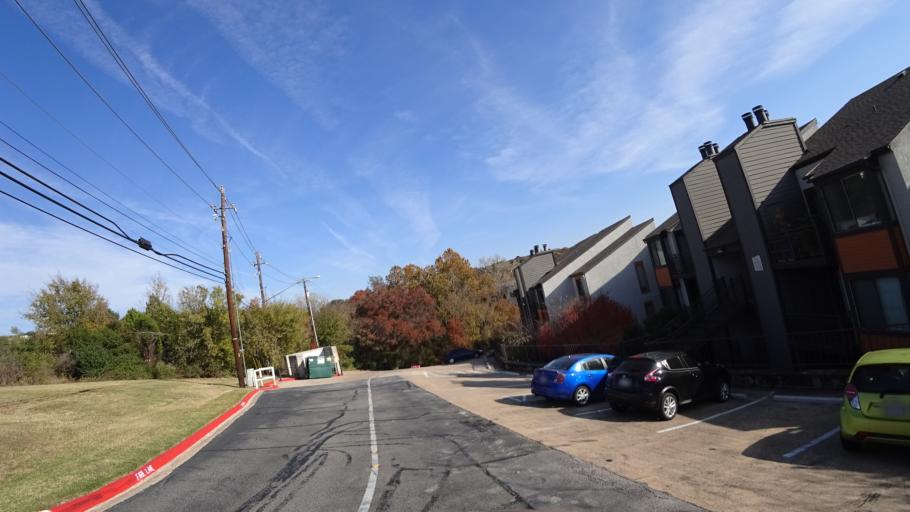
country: US
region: Texas
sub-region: Williamson County
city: Jollyville
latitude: 30.3876
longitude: -97.7620
